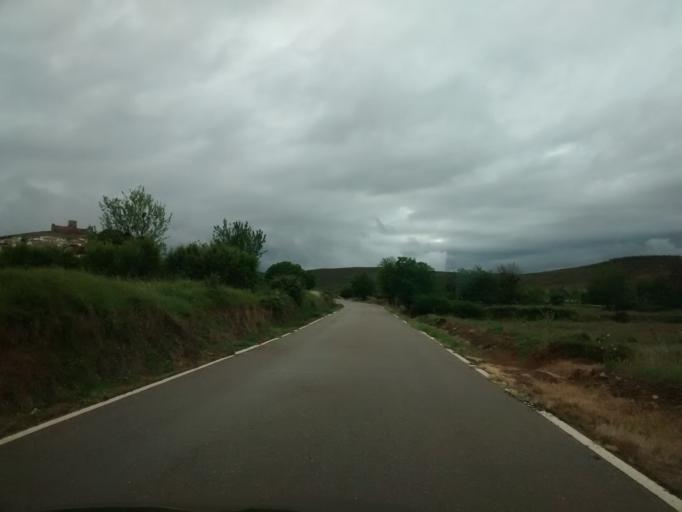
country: ES
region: Aragon
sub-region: Provincia de Zaragoza
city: Trasmoz
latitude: 41.8277
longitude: -1.7129
